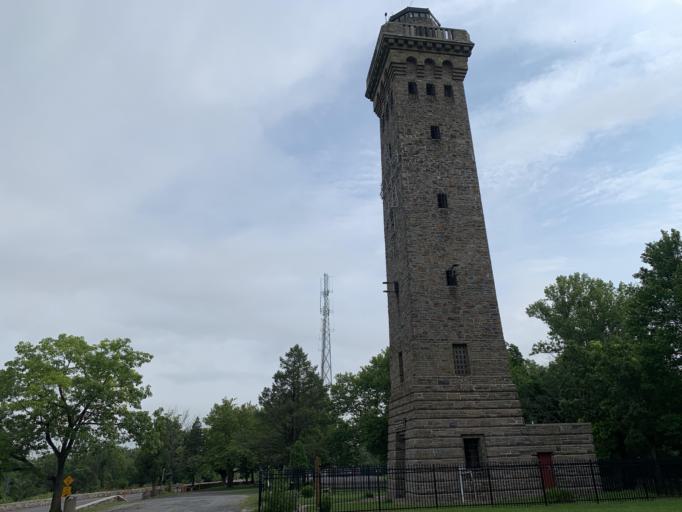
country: US
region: Pennsylvania
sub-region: Berks County
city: Mount Penn
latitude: 40.3470
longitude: -75.9027
